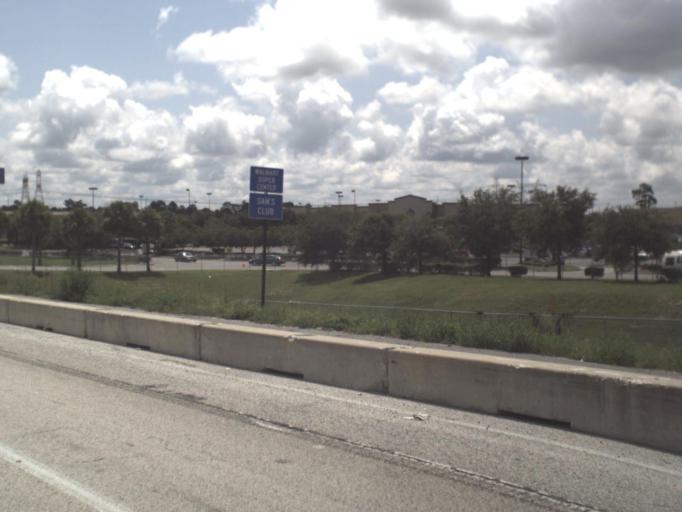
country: US
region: Florida
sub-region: Hernando County
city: High Point
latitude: 28.5336
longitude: -82.5064
